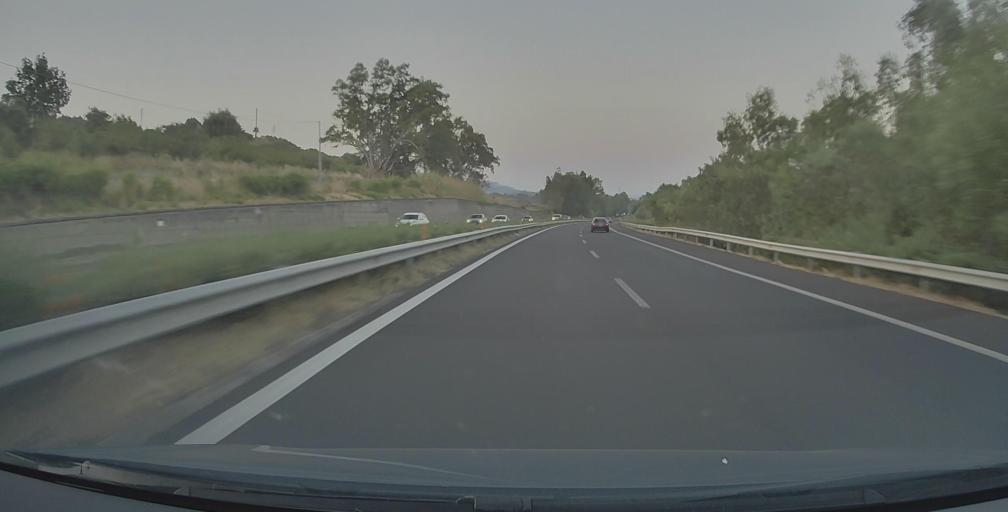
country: IT
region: Sicily
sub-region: Catania
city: Pasteria-Lapide
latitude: 37.8143
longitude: 15.2149
